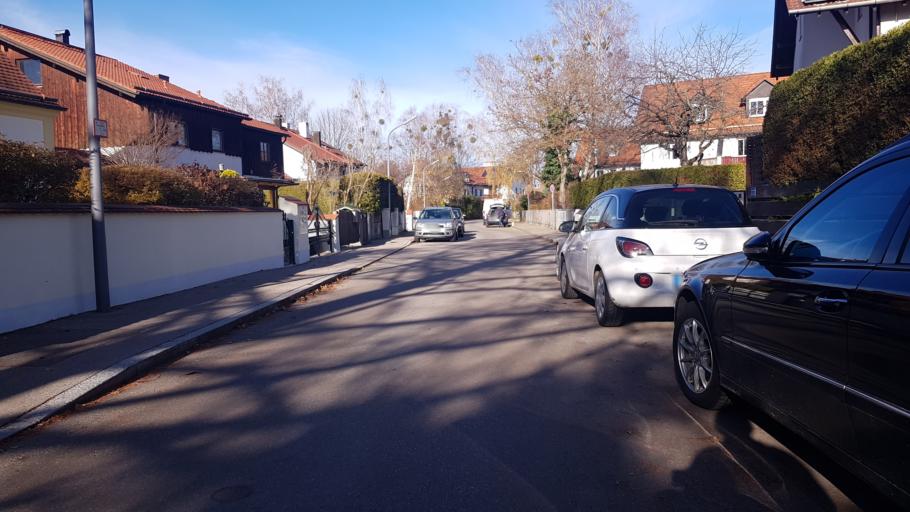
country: DE
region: Bavaria
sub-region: Upper Bavaria
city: Karlsfeld
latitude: 48.1974
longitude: 11.5122
